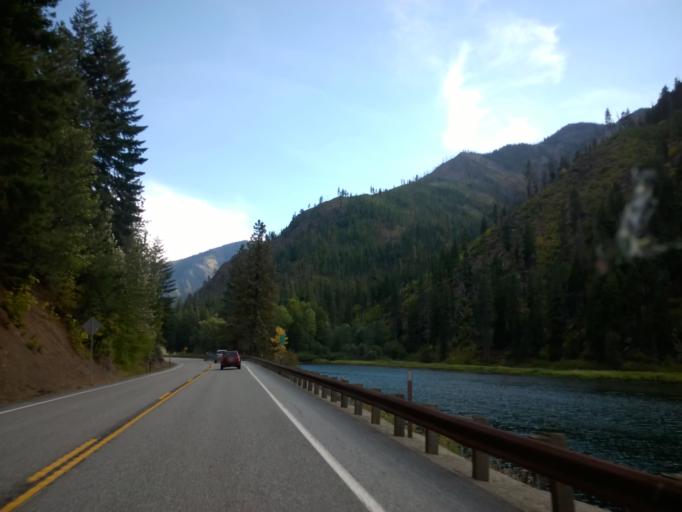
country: US
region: Washington
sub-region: Chelan County
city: Leavenworth
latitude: 47.6197
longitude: -120.7241
